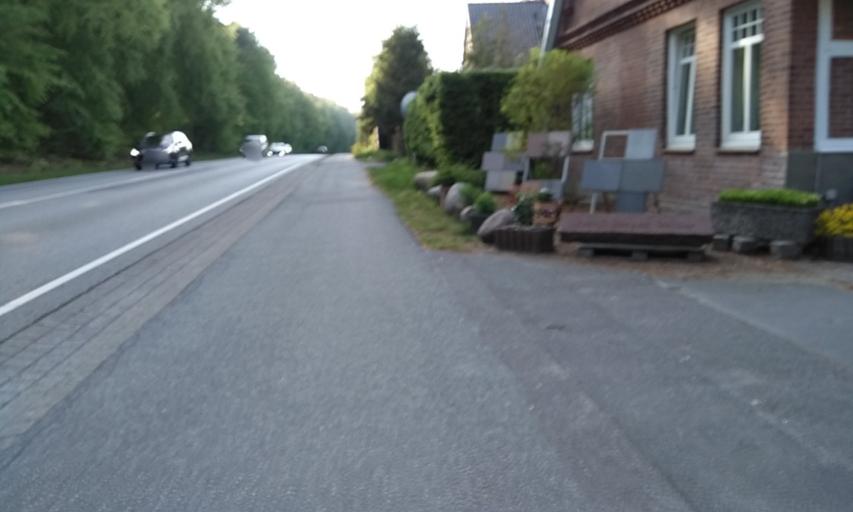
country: DE
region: Lower Saxony
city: Buxtehude
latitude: 53.4728
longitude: 9.6573
